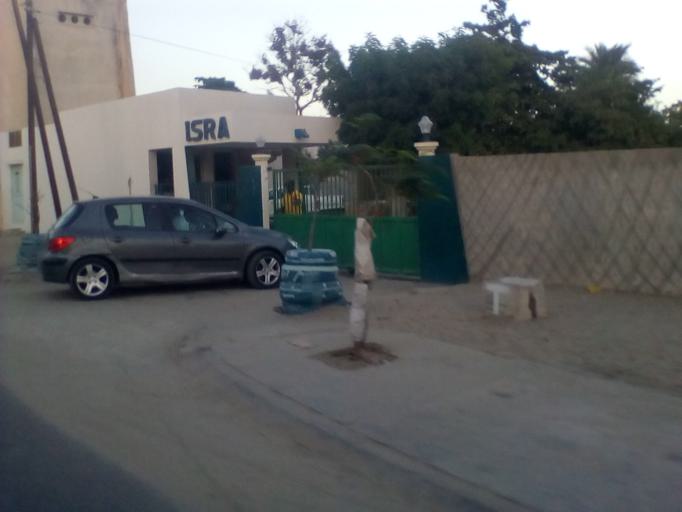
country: SN
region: Saint-Louis
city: Saint-Louis
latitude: 16.0129
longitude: -16.4887
